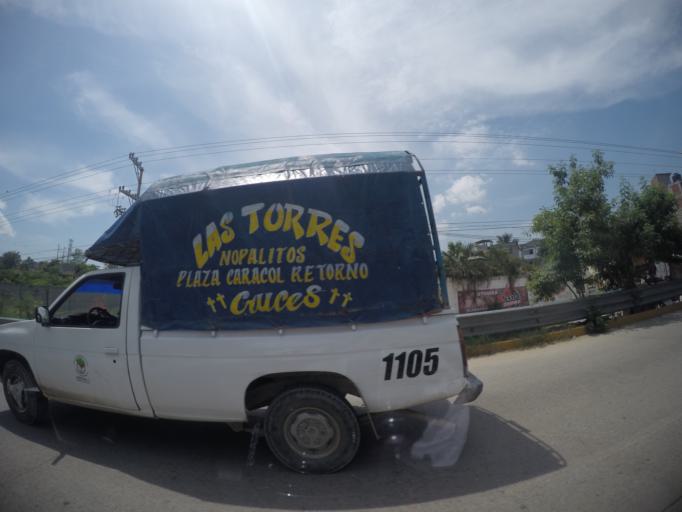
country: MX
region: Guerrero
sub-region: Acapulco de Juarez
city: Colonia Nueva Revolucion
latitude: 16.9149
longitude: -99.8230
